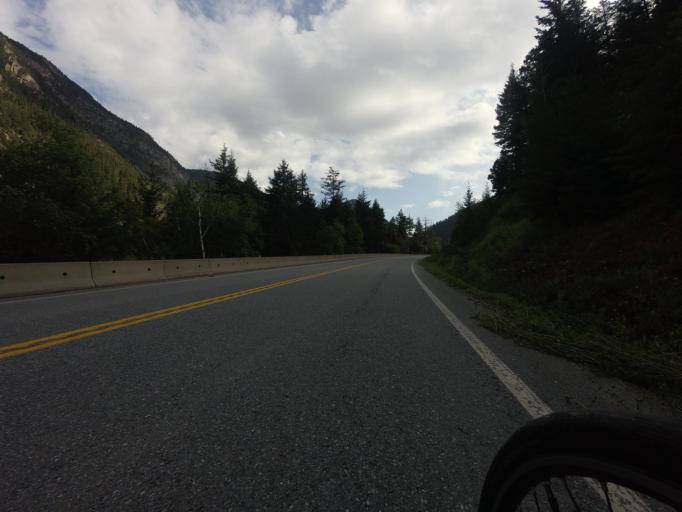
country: CA
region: British Columbia
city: Lillooet
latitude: 50.6300
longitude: -122.0926
